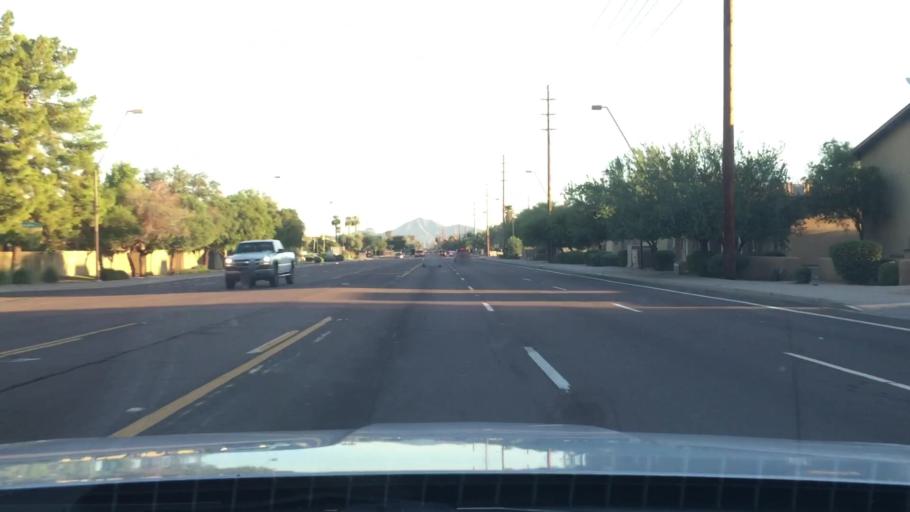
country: US
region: Arizona
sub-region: Maricopa County
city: Guadalupe
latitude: 33.3900
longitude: -111.9608
